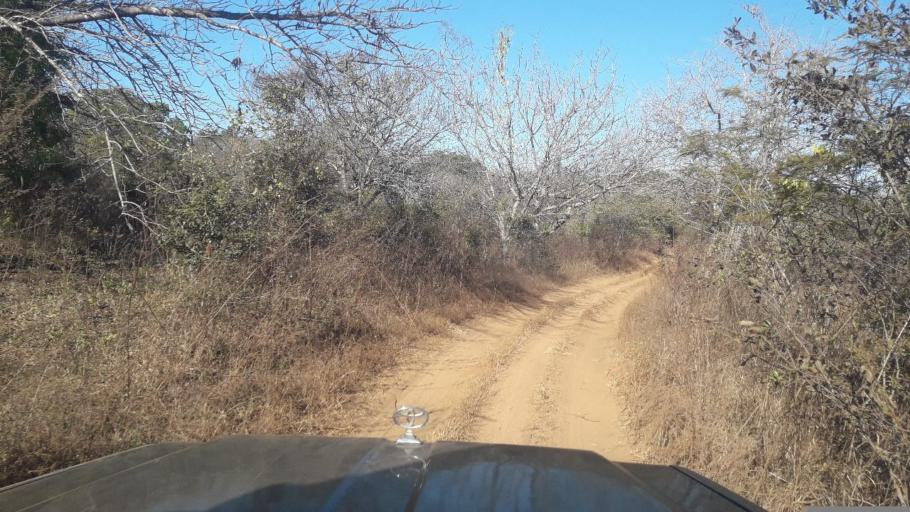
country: MG
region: Boeny
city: Sitampiky
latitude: -16.4194
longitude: 45.6161
